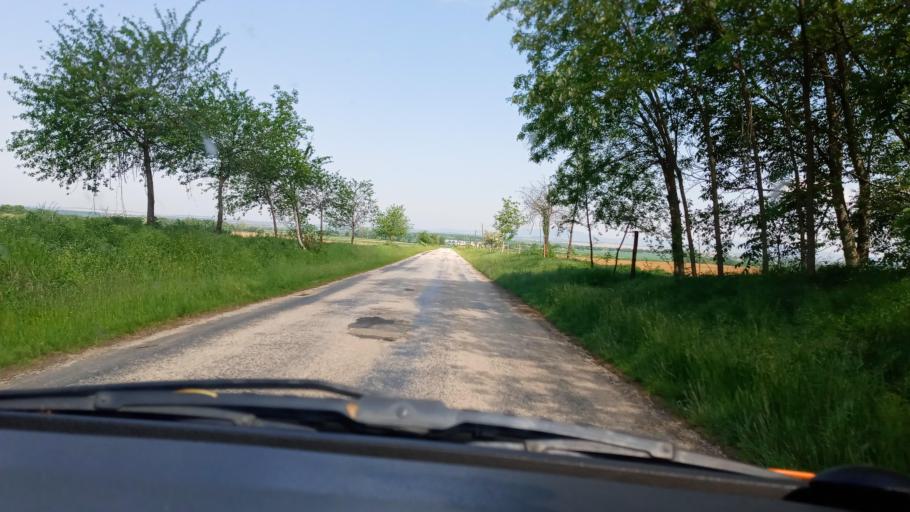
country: HU
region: Baranya
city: Harkany
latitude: 45.9091
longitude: 18.2455
